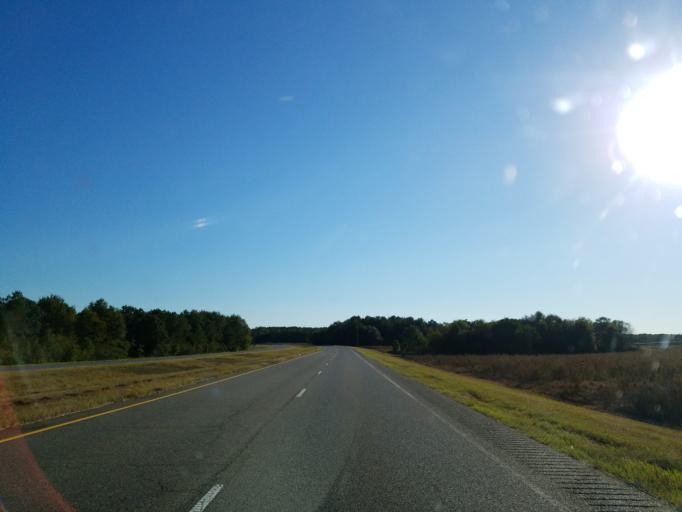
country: US
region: Georgia
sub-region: Lee County
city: Leesburg
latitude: 31.7371
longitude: -84.1792
